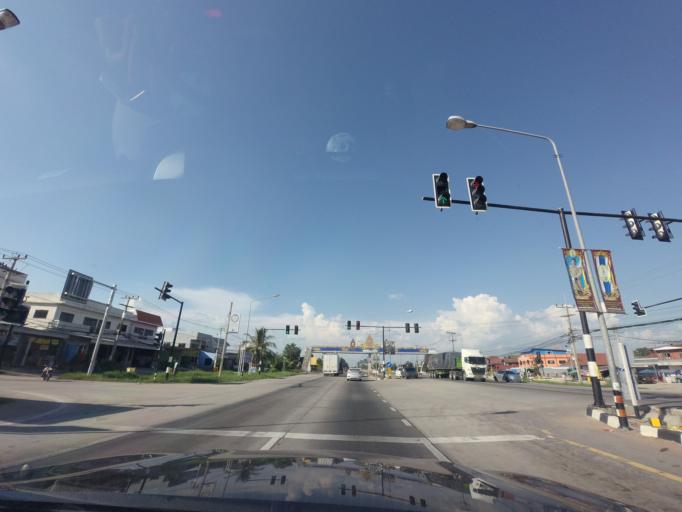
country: TH
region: Khon Kaen
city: Non Sila
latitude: 15.9661
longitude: 102.6913
